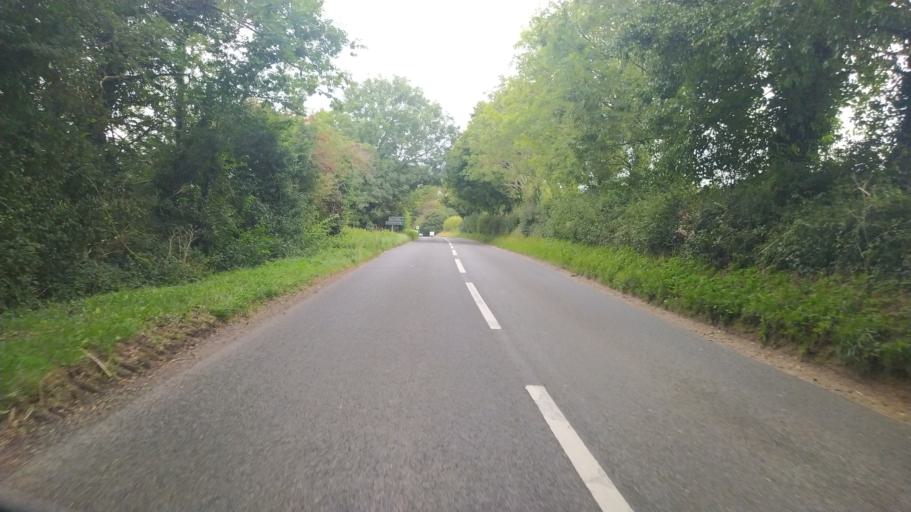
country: GB
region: England
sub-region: Dorset
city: Dorchester
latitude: 50.7633
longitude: -2.3905
